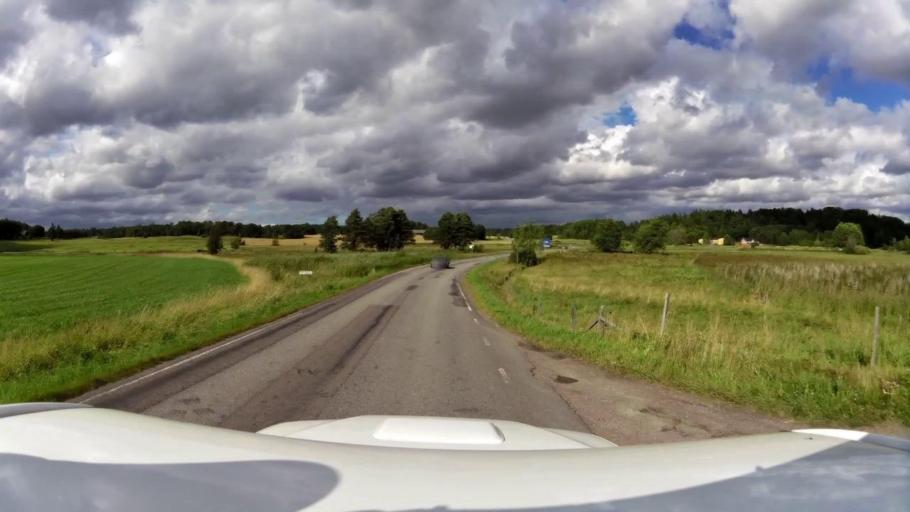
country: SE
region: OEstergoetland
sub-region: Linkopings Kommun
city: Sturefors
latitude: 58.3280
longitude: 15.7141
